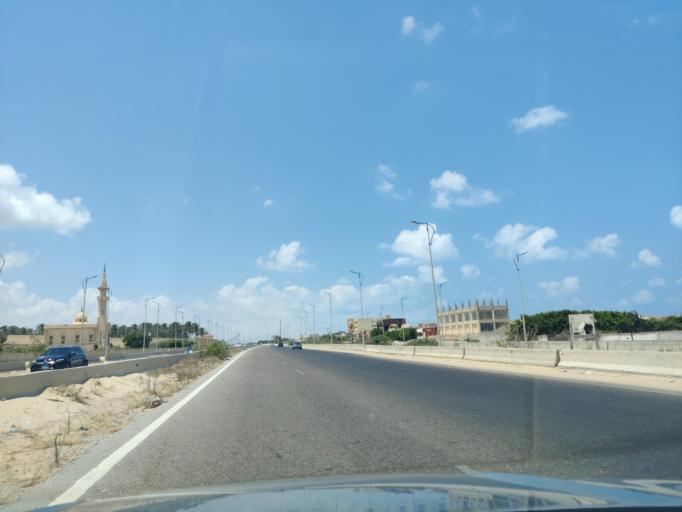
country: EG
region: Alexandria
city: Alexandria
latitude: 30.9873
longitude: 29.5888
